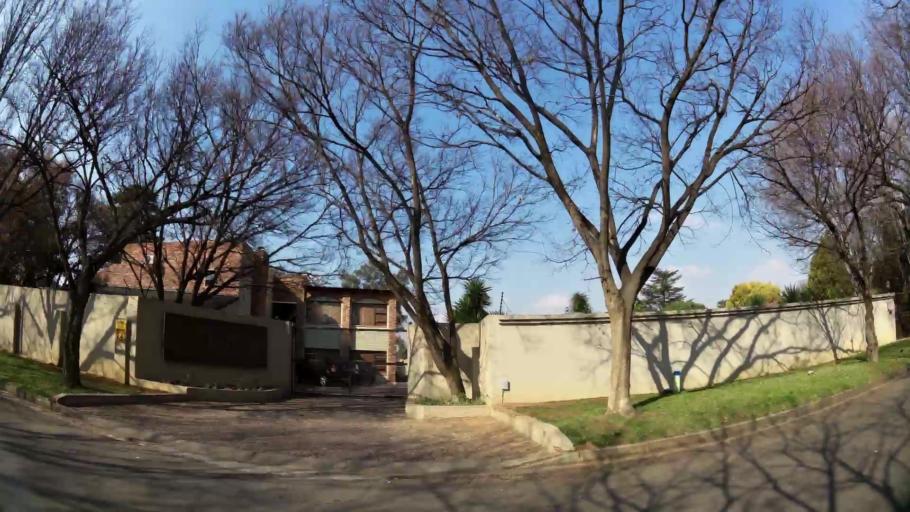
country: ZA
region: Gauteng
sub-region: Ekurhuleni Metropolitan Municipality
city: Boksburg
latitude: -26.1806
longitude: 28.2743
